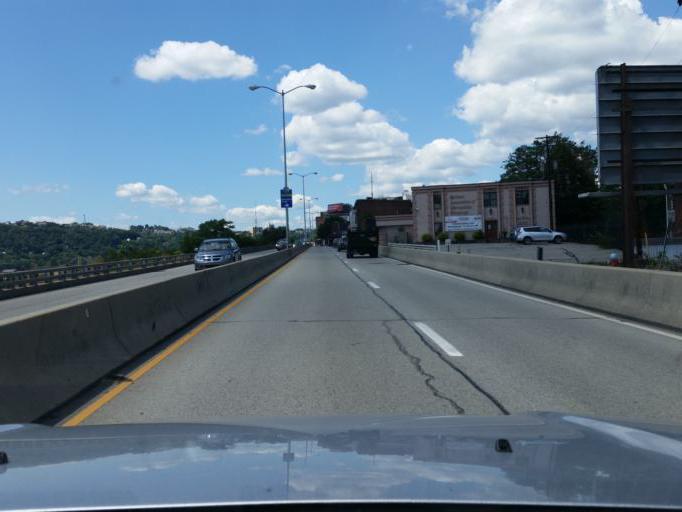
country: US
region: Pennsylvania
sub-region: Allegheny County
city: Pittsburgh
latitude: 40.4365
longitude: -79.9757
